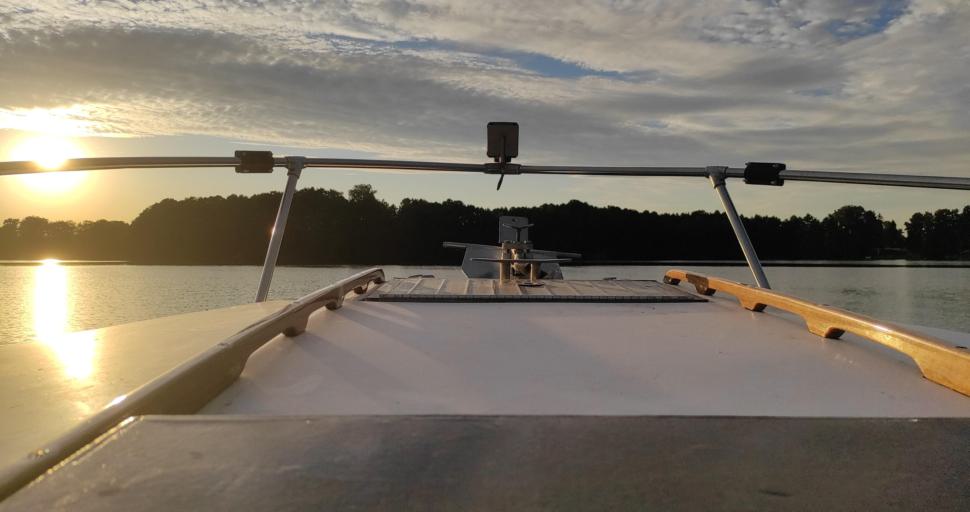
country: DE
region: Brandenburg
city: Friedland
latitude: 52.0220
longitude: 14.1854
